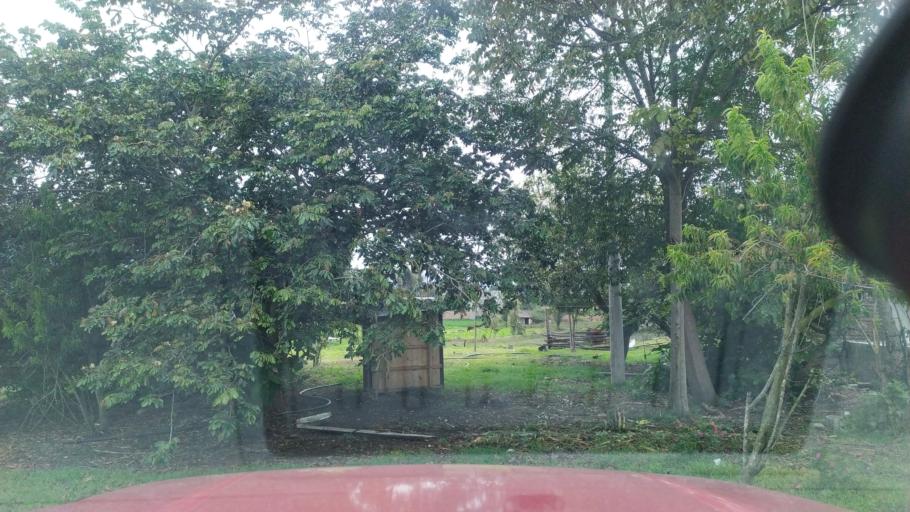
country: EC
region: Chimborazo
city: Riobamba
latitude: -1.6545
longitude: -78.6392
